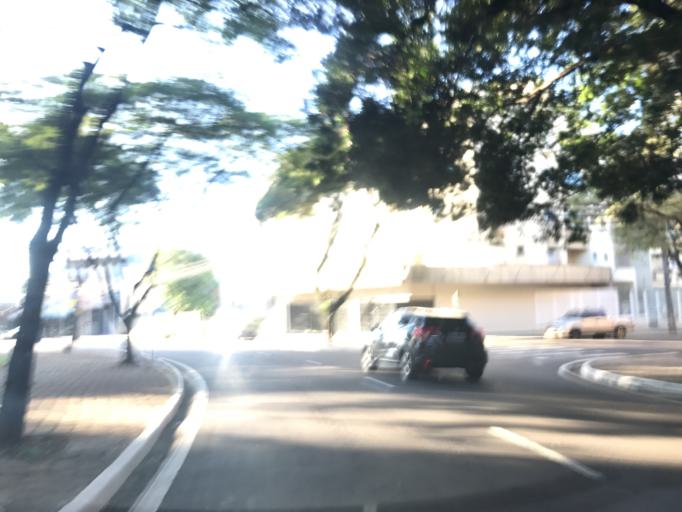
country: BR
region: Parana
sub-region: Maringa
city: Maringa
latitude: -23.4259
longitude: -51.9487
